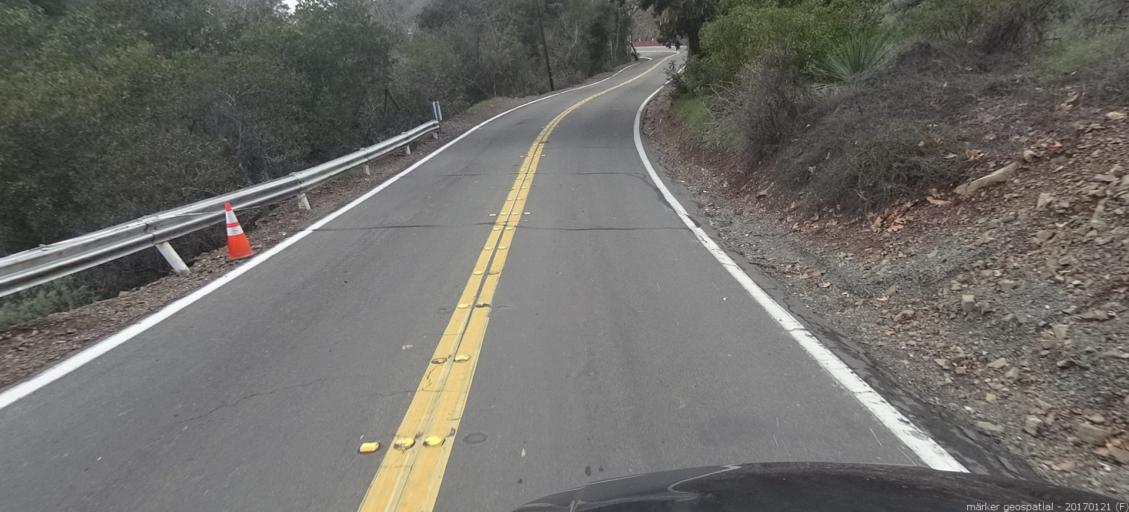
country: US
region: California
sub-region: Orange County
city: Portola Hills
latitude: 33.7456
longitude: -117.5858
